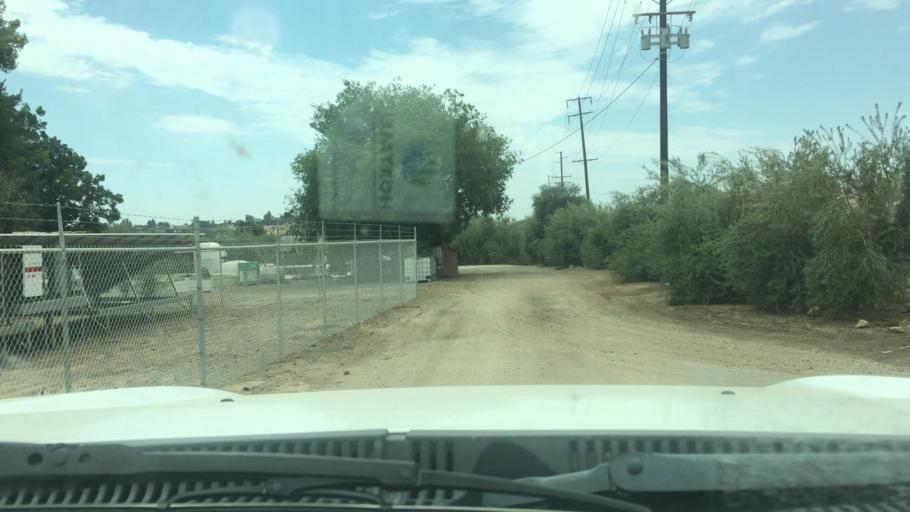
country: US
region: California
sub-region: Tulare County
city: Porterville
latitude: 36.0949
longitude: -119.0061
